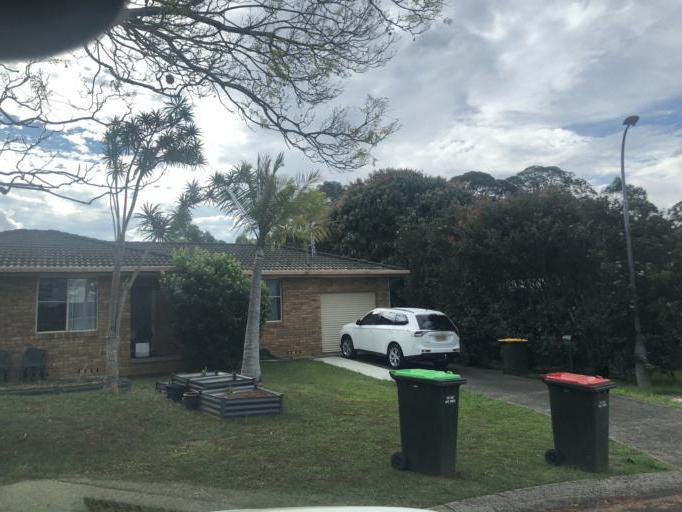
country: AU
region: New South Wales
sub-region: Coffs Harbour
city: Coffs Harbour
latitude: -30.2908
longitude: 153.0999
